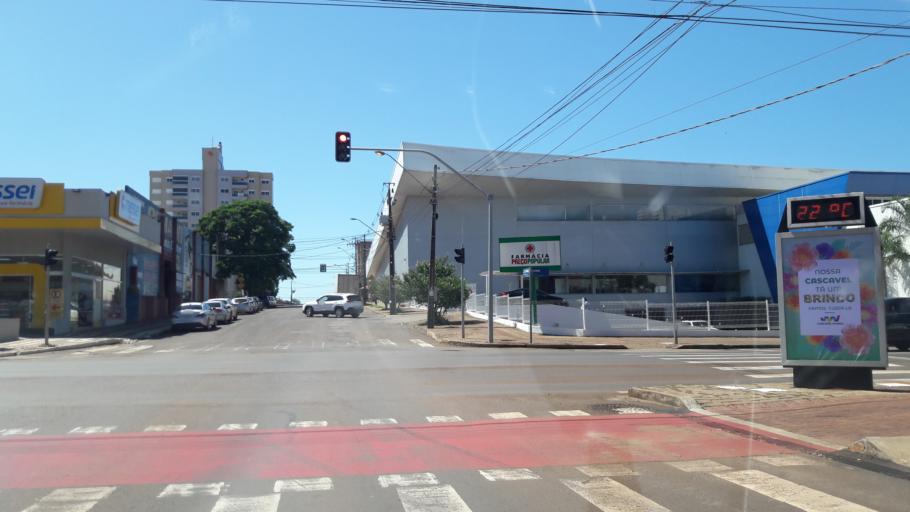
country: BR
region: Parana
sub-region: Cascavel
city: Cascavel
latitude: -24.9504
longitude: -53.4459
